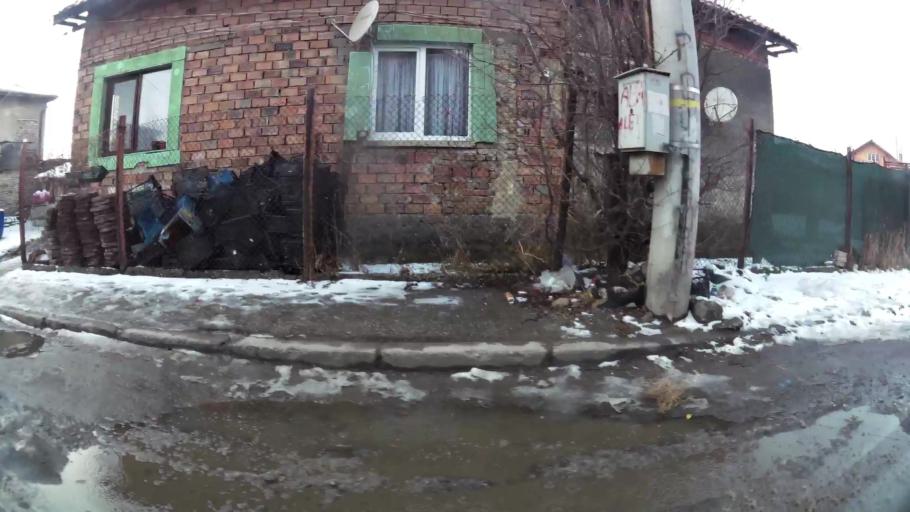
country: BG
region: Sofia-Capital
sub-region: Stolichna Obshtina
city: Sofia
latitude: 42.6890
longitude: 23.3820
